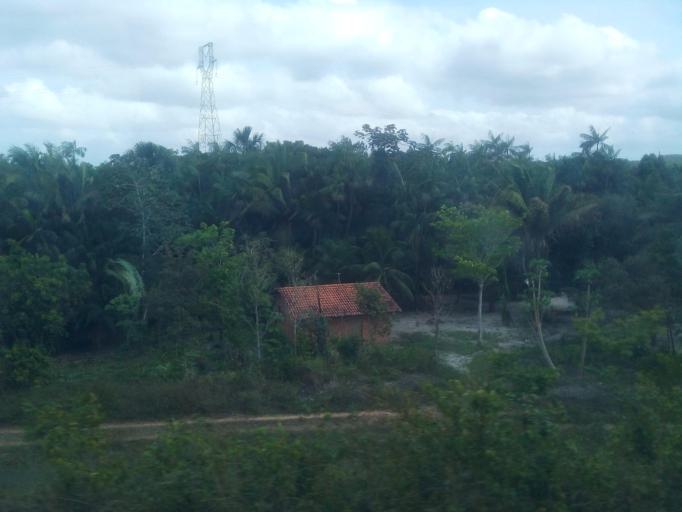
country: BR
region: Maranhao
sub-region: Sao Luis
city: Sao Luis
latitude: -2.7336
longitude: -44.3460
